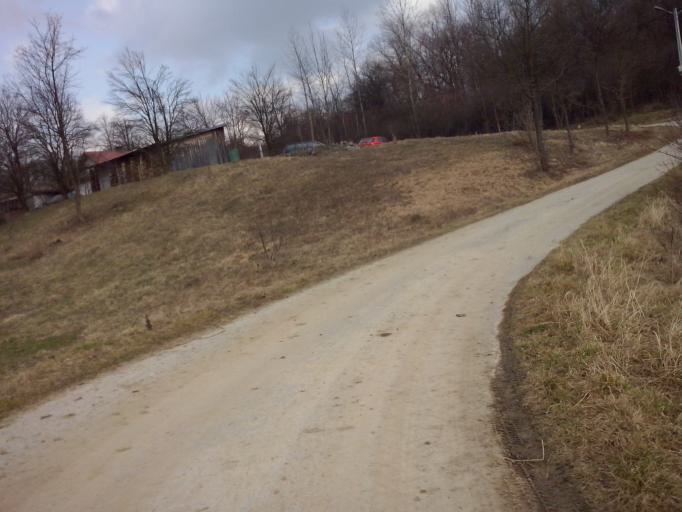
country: PL
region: Subcarpathian Voivodeship
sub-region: Powiat nizanski
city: Krzeszow
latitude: 50.4162
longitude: 22.3266
